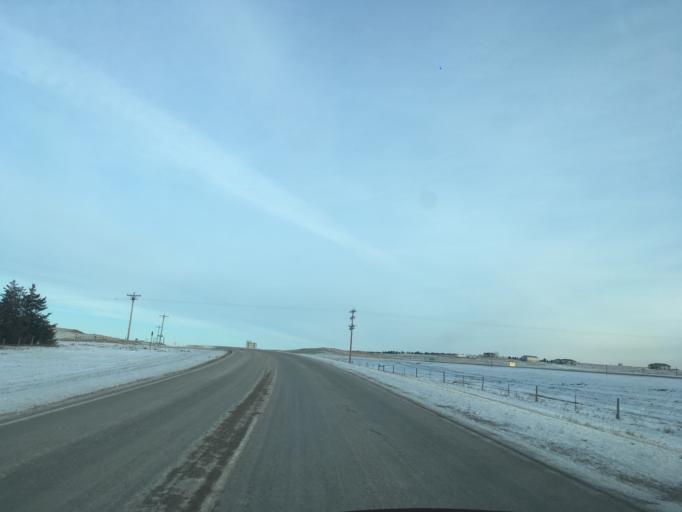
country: US
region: South Dakota
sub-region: Lawrence County
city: North Spearfish
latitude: 44.5470
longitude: -104.0083
